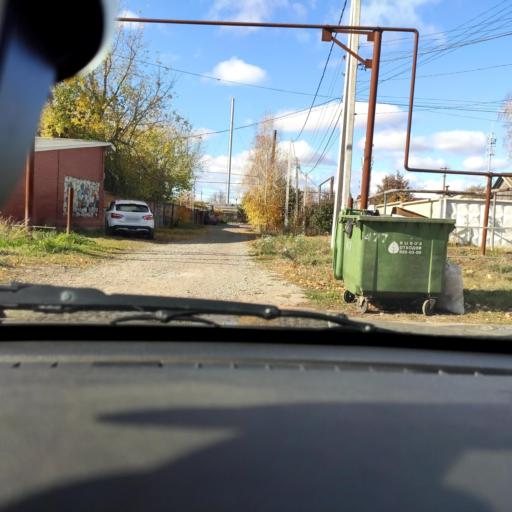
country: RU
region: Samara
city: Podstepki
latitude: 53.5100
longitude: 49.2318
